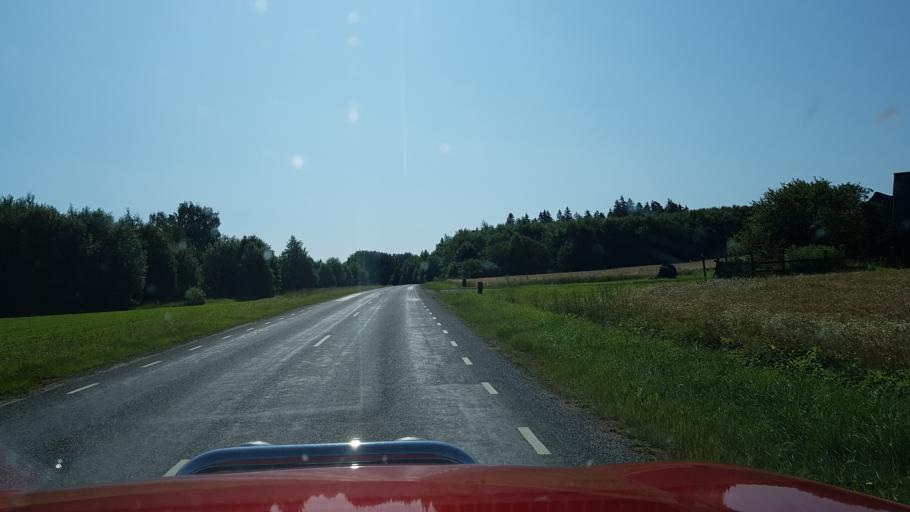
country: EE
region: Vorumaa
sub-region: Voru linn
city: Voru
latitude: 57.9753
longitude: 26.8242
